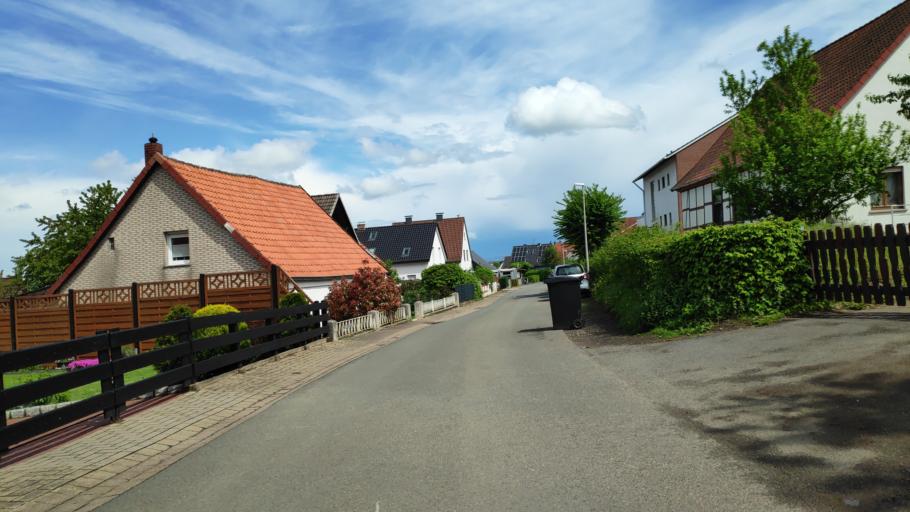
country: DE
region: North Rhine-Westphalia
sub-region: Regierungsbezirk Detmold
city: Minden
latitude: 52.2690
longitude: 8.8880
